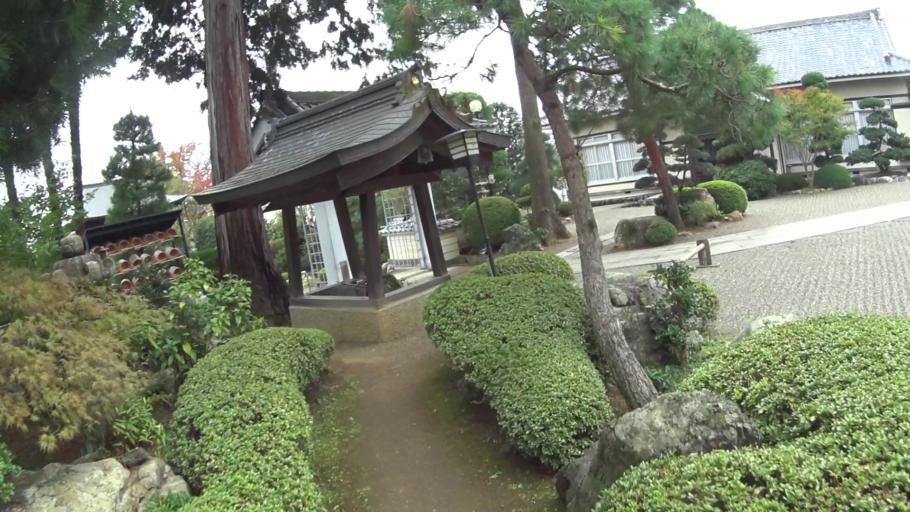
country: JP
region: Saitama
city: Hanno
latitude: 35.8606
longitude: 139.3198
